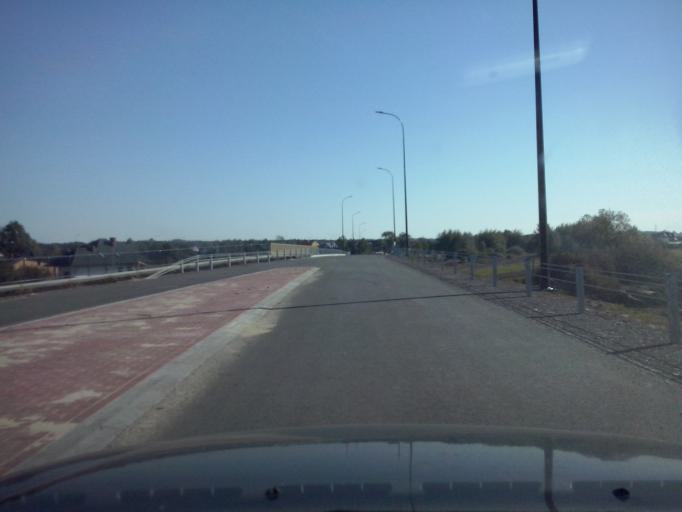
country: PL
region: Lublin Voivodeship
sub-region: Powiat bilgorajski
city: Bilgoraj
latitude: 50.5214
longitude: 22.7104
